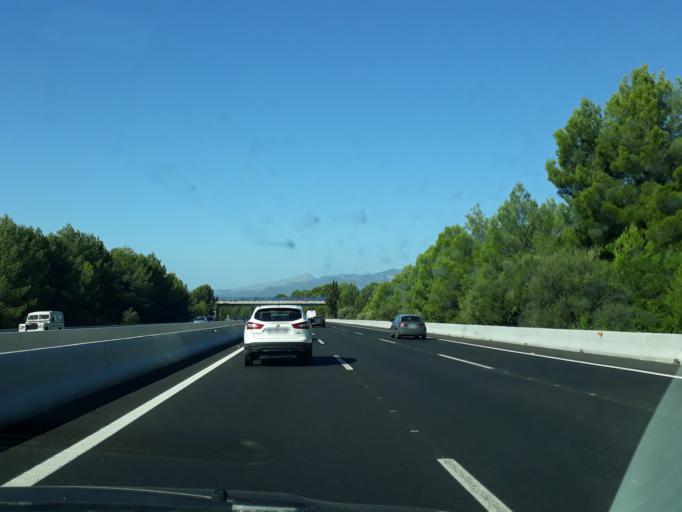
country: ES
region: Balearic Islands
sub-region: Illes Balears
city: Marratxi
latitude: 39.6300
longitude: 2.7286
